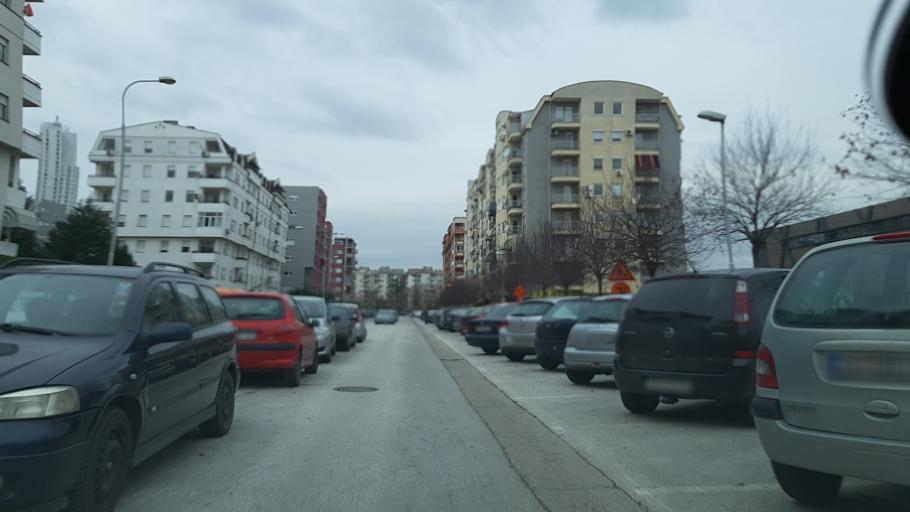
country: MK
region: Kisela Voda
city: Usje
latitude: 41.9801
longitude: 21.4731
